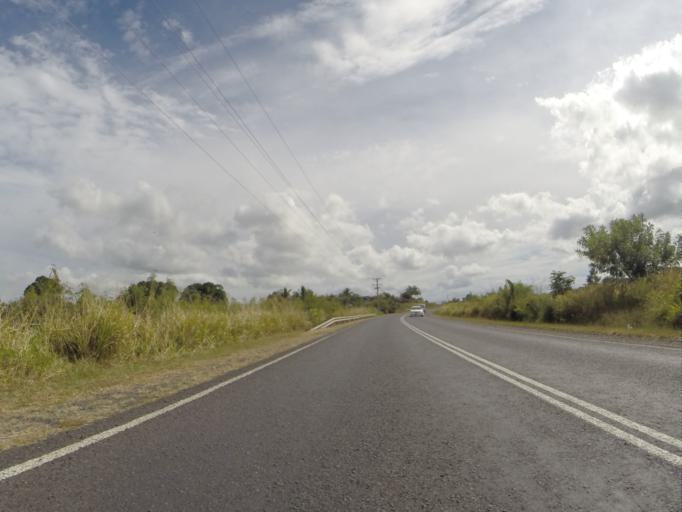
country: FJ
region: Western
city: Nadi
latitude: -18.1113
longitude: 177.4053
